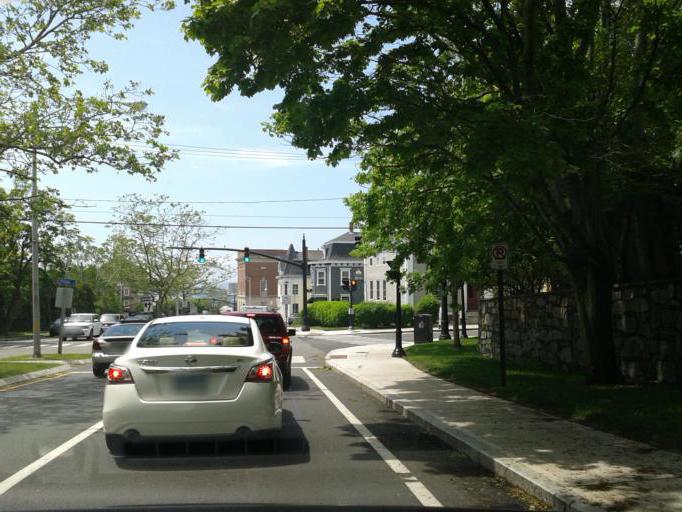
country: US
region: Rhode Island
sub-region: Newport County
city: Newport
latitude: 41.4843
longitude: -71.3126
